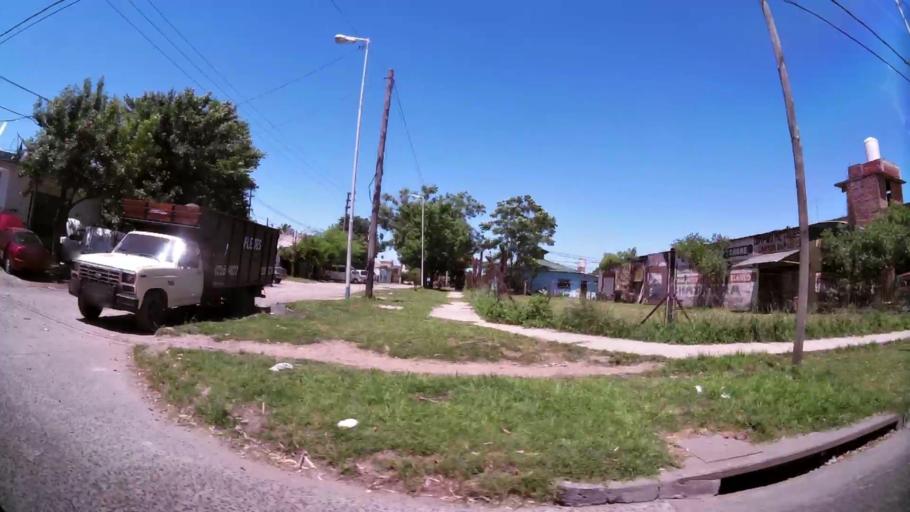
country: AR
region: Buenos Aires
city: Hurlingham
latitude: -34.5078
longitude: -58.7012
